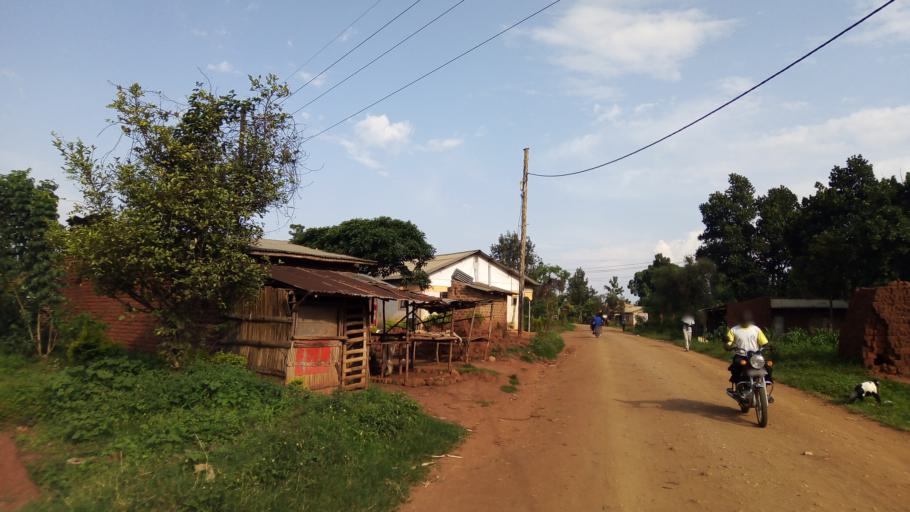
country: UG
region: Eastern Region
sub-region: Mbale District
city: Mbale
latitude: 1.0609
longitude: 34.1547
